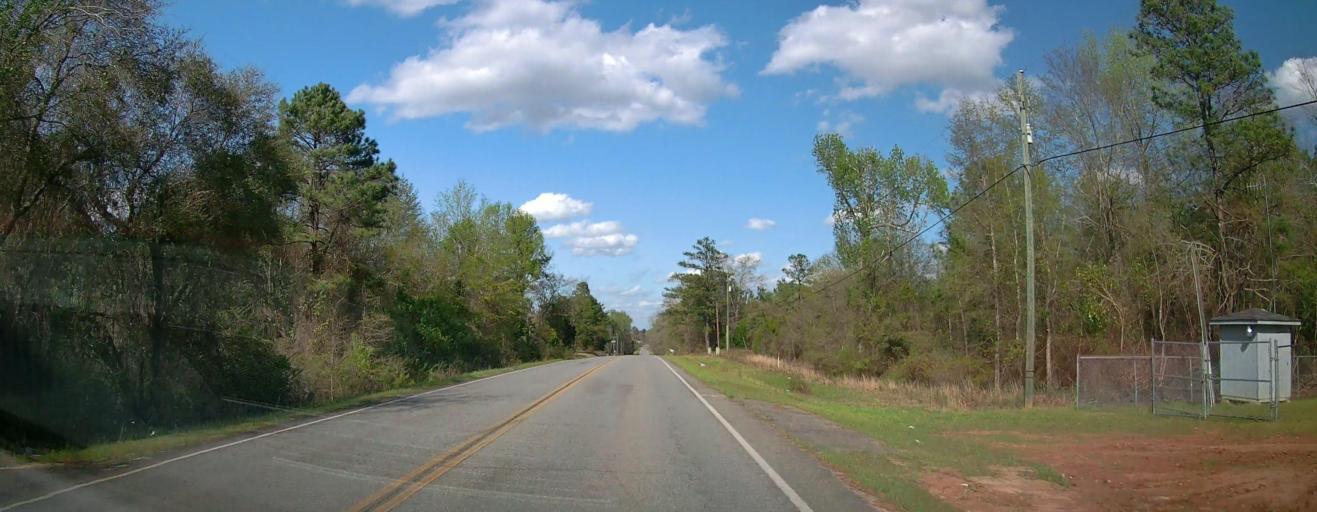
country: US
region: Georgia
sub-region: Baldwin County
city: Hardwick
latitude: 32.9847
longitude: -83.2720
